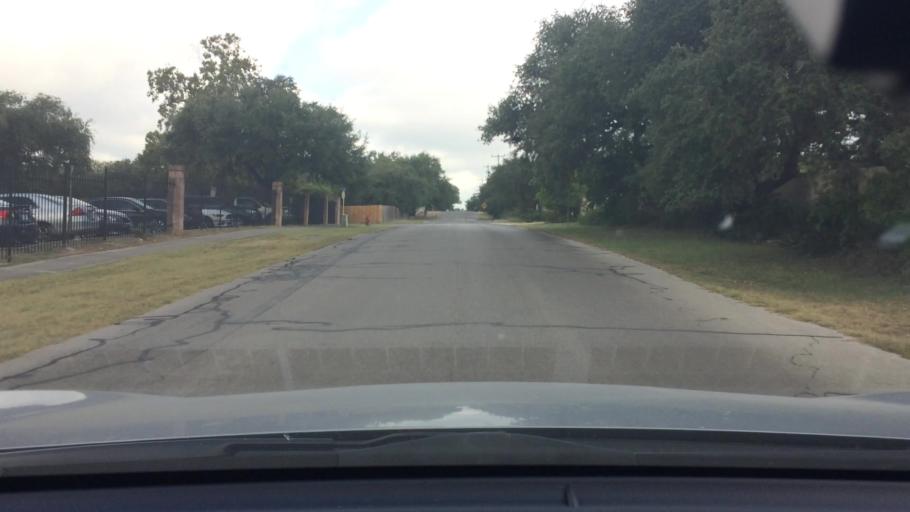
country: US
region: Texas
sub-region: Bexar County
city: Hollywood Park
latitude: 29.5582
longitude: -98.4707
